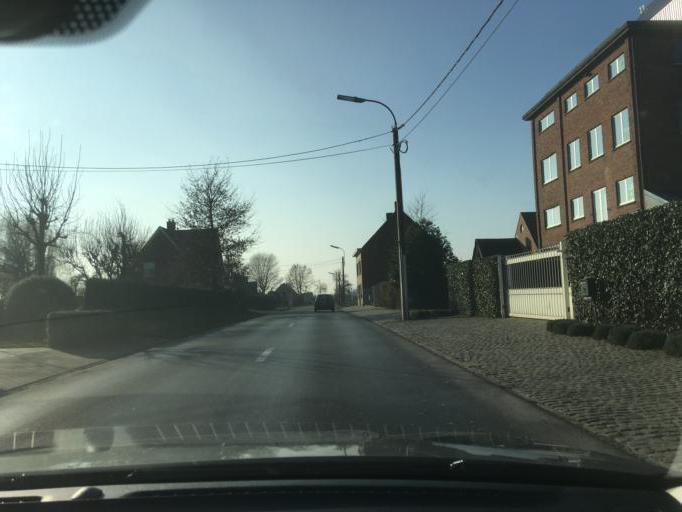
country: BE
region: Flanders
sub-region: Provincie West-Vlaanderen
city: Ledegem
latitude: 50.9021
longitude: 3.1431
